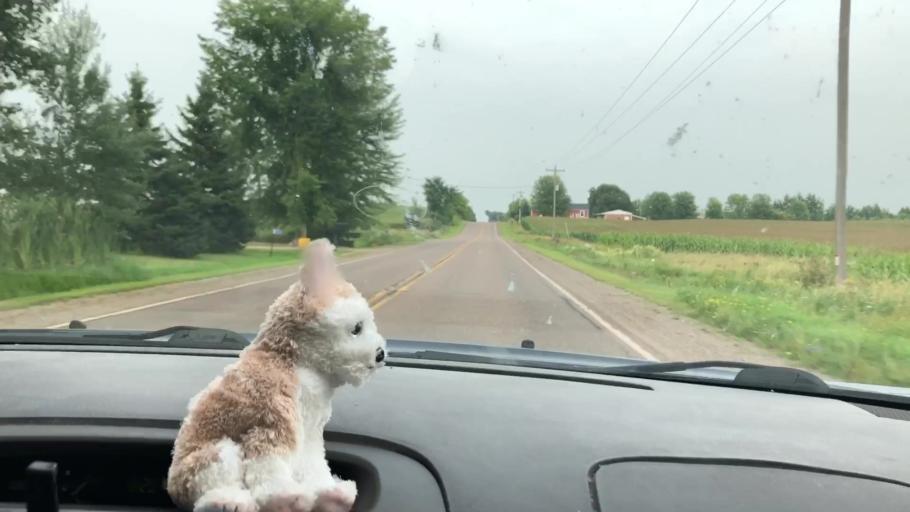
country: US
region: Wisconsin
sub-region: Chippewa County
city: Stanley
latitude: 44.9597
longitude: -90.8793
